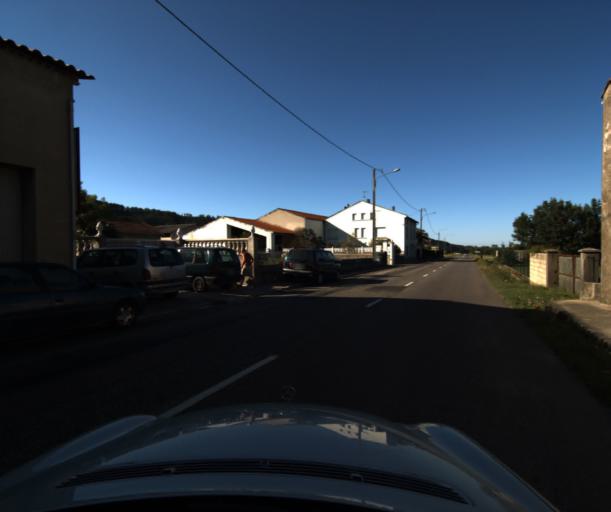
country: FR
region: Midi-Pyrenees
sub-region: Departement de l'Ariege
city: Lavelanet
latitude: 42.9966
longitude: 1.8793
